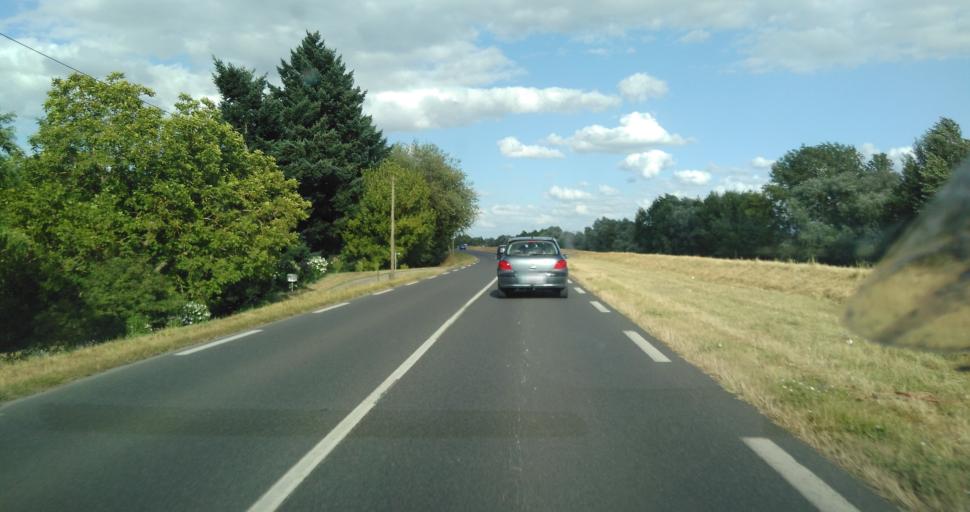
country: FR
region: Centre
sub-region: Departement d'Indre-et-Loire
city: Fondettes
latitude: 47.3845
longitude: 0.5925
